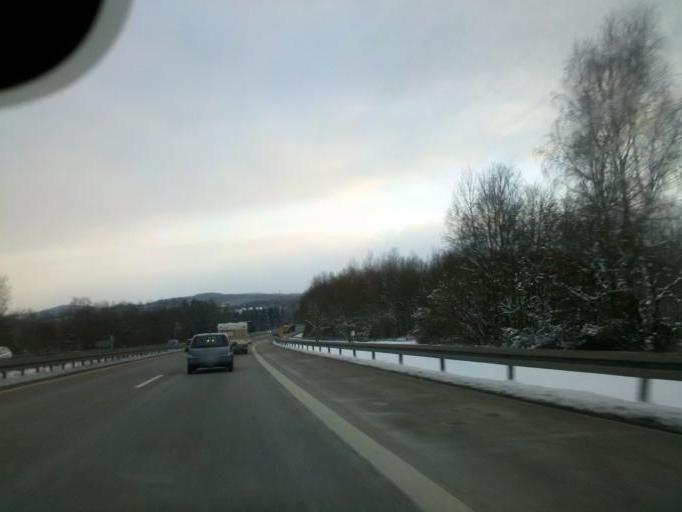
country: DE
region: North Rhine-Westphalia
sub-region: Regierungsbezirk Arnsberg
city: Olpe
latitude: 51.0336
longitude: 7.8195
